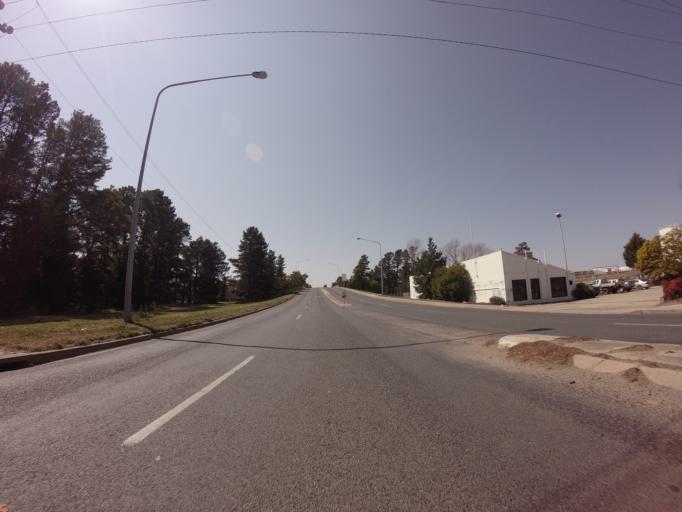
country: AU
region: Australian Capital Territory
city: Forrest
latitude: -35.3274
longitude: 149.1642
